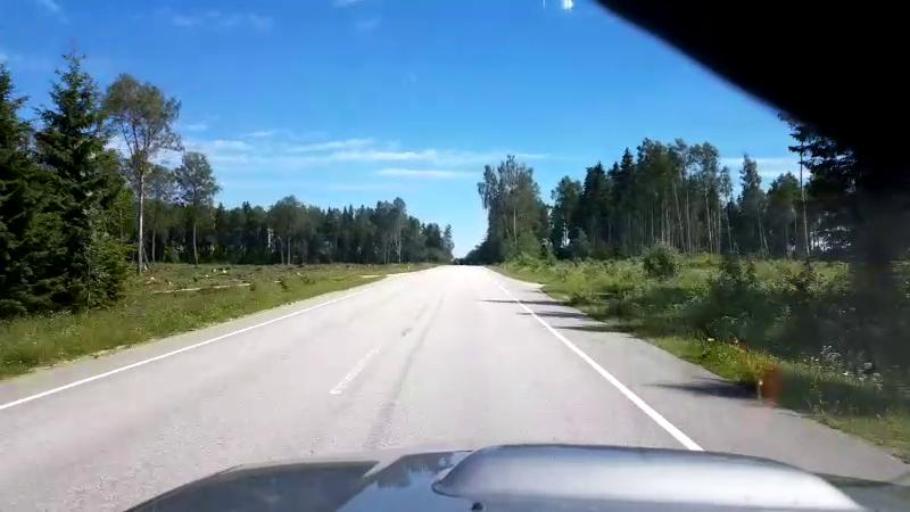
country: EE
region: Jaervamaa
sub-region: Koeru vald
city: Koeru
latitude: 58.9940
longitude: 25.9560
